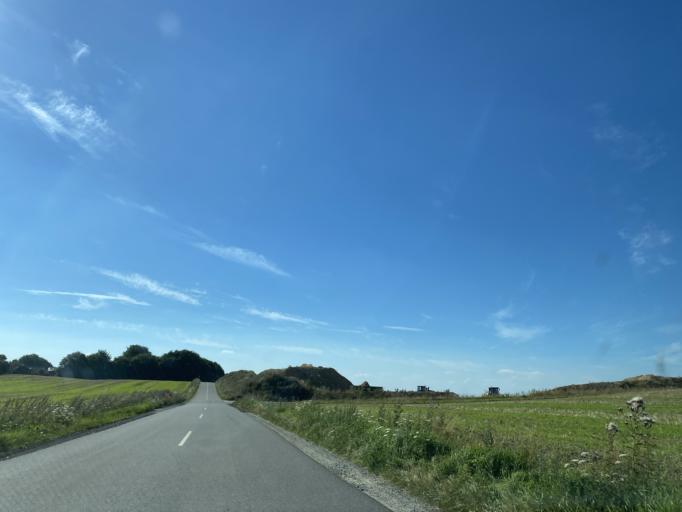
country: DK
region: South Denmark
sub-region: Vejle Kommune
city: Give
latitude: 55.8739
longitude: 9.3313
